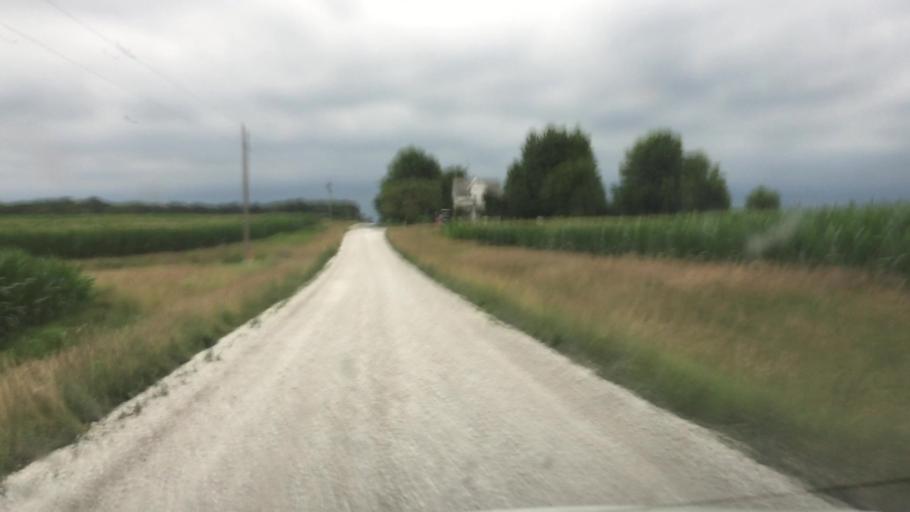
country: US
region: Illinois
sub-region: Adams County
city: Camp Point
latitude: 40.2156
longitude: -90.9678
